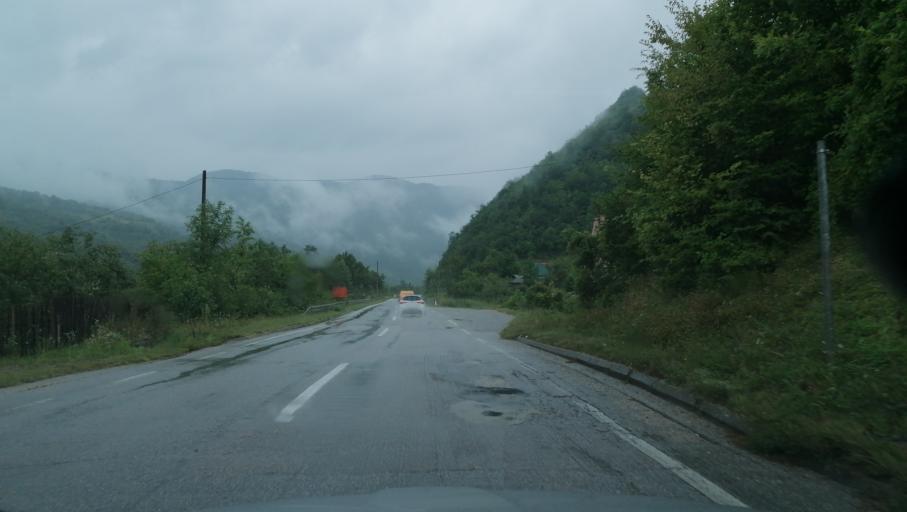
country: BA
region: Republika Srpska
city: Visegrad
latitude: 43.7141
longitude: 19.1684
